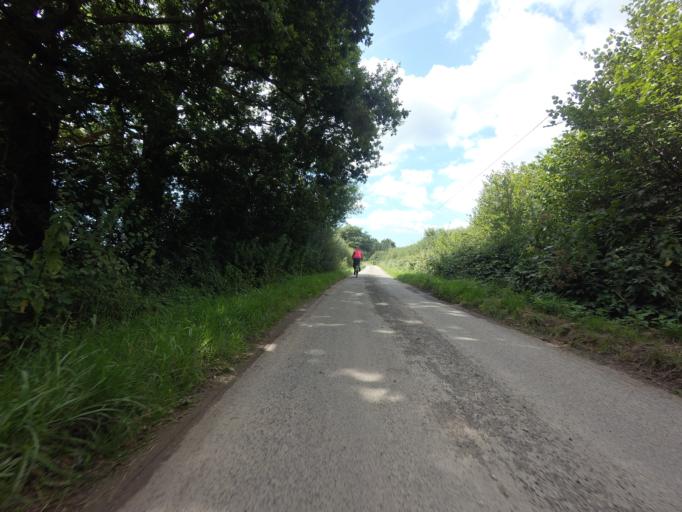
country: GB
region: England
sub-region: Kent
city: Stone
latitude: 51.0663
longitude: 0.7594
